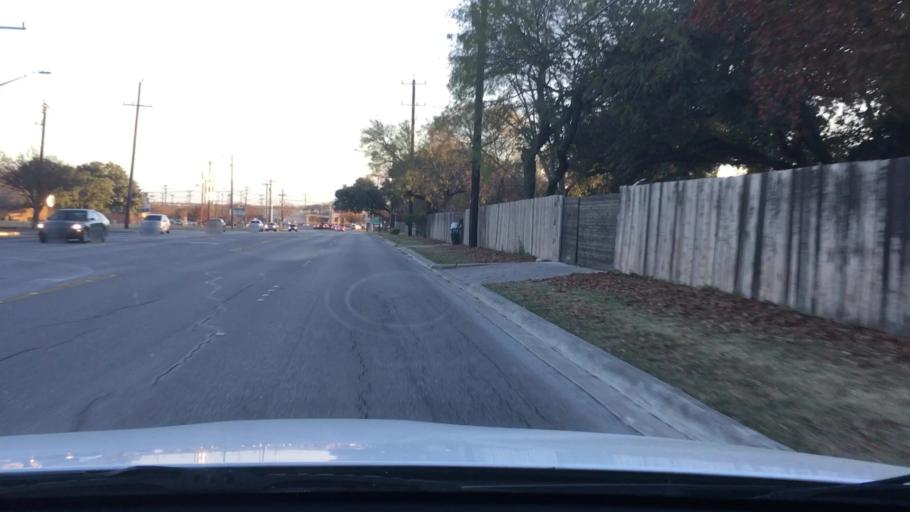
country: US
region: Texas
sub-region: Bexar County
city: Windcrest
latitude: 29.5135
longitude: -98.3718
